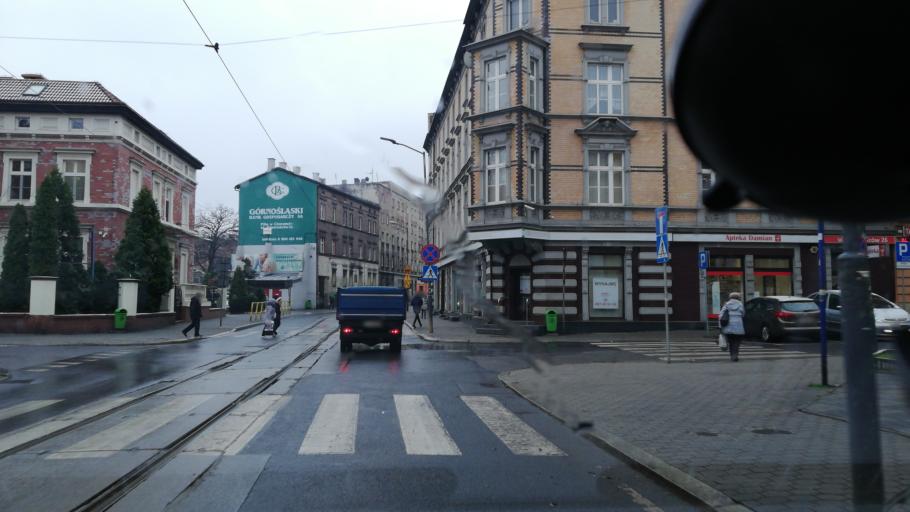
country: PL
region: Silesian Voivodeship
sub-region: Chorzow
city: Chorzow
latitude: 50.2939
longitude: 18.9502
